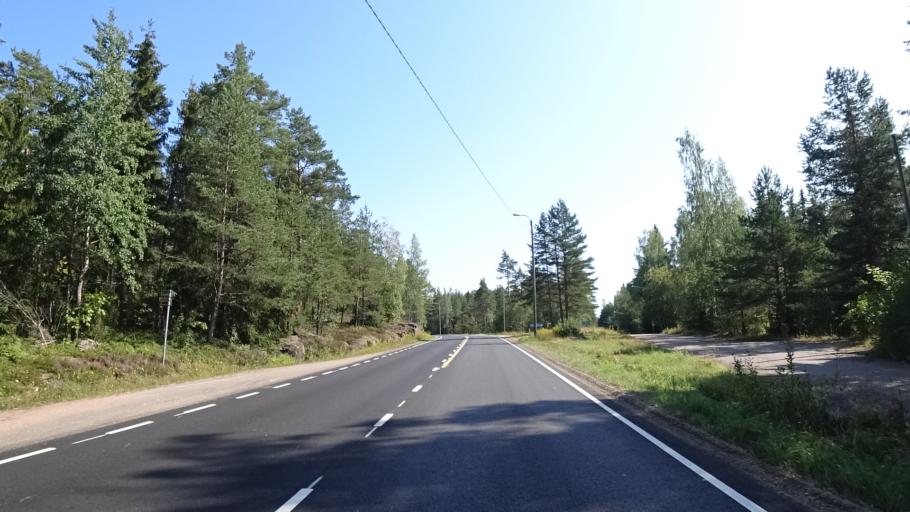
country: FI
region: Kymenlaakso
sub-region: Kotka-Hamina
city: Karhula
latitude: 60.5555
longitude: 26.8981
